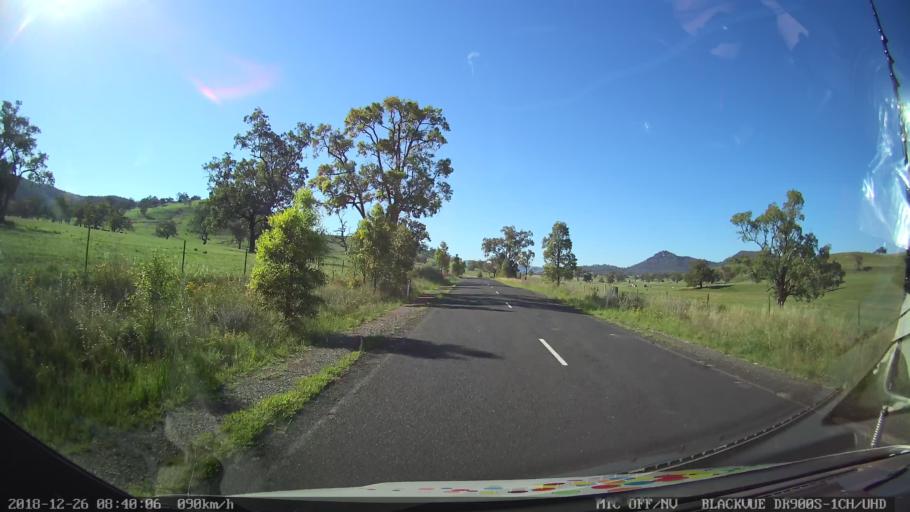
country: AU
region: New South Wales
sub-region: Mid-Western Regional
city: Kandos
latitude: -32.4625
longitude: 150.0759
